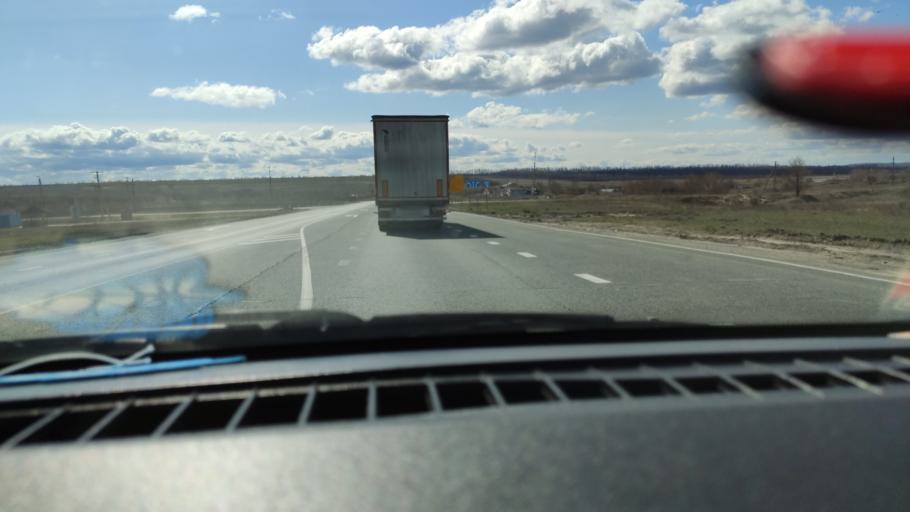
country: RU
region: Saratov
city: Dukhovnitskoye
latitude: 52.7416
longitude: 48.2536
